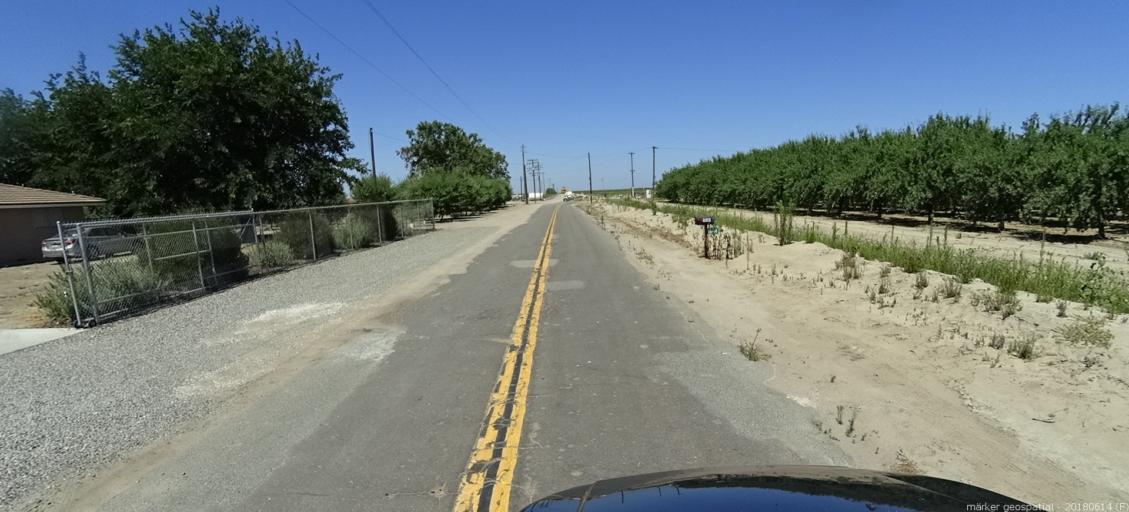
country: US
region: California
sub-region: Madera County
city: Fairmead
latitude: 36.9892
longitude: -120.2464
